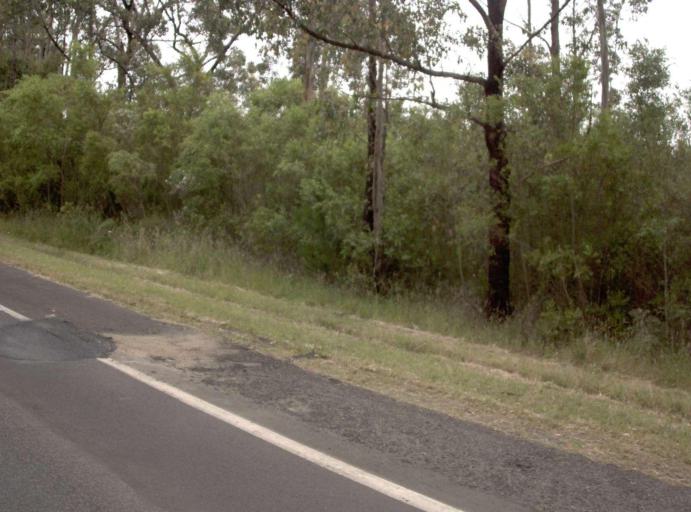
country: AU
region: Victoria
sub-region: Latrobe
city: Moe
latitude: -38.3027
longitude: 146.2801
